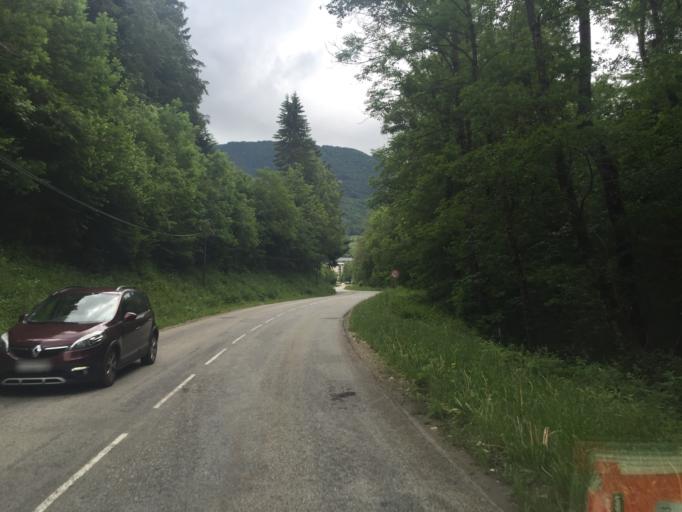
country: FR
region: Rhone-Alpes
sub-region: Departement de la Savoie
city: Cruet
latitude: 45.6119
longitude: 6.0952
